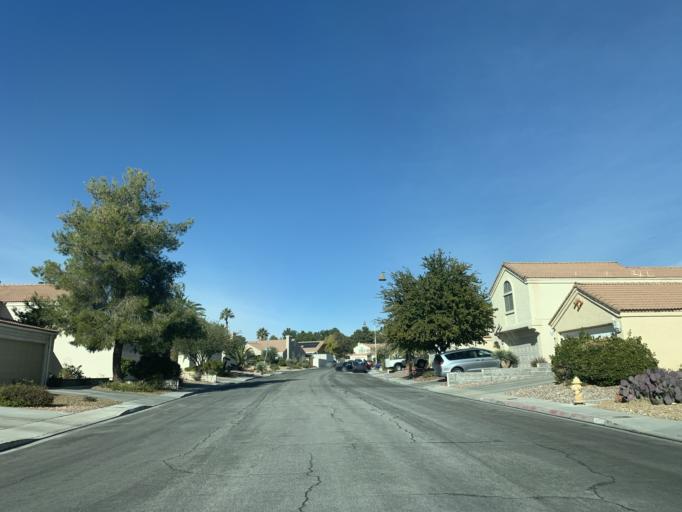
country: US
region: Nevada
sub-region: Clark County
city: Summerlin South
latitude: 36.1313
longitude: -115.2937
